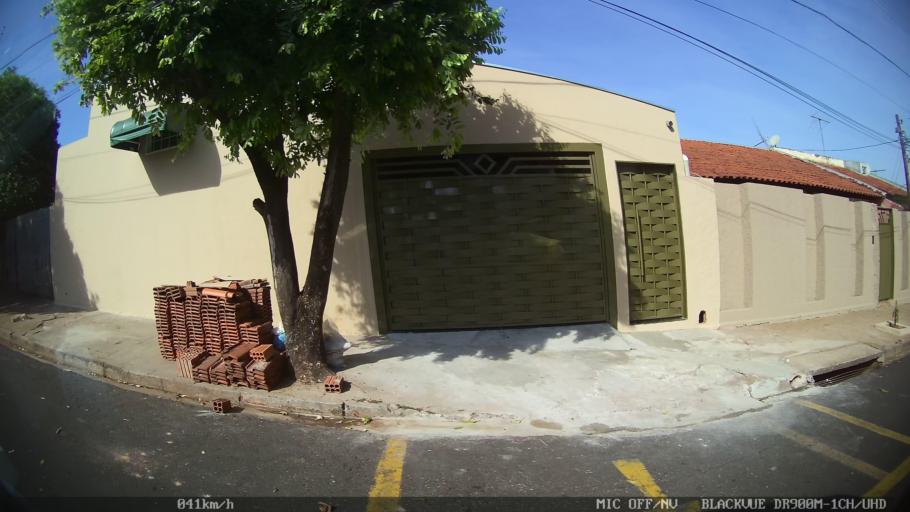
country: BR
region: Sao Paulo
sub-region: Sao Jose Do Rio Preto
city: Sao Jose do Rio Preto
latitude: -20.7974
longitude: -49.4170
